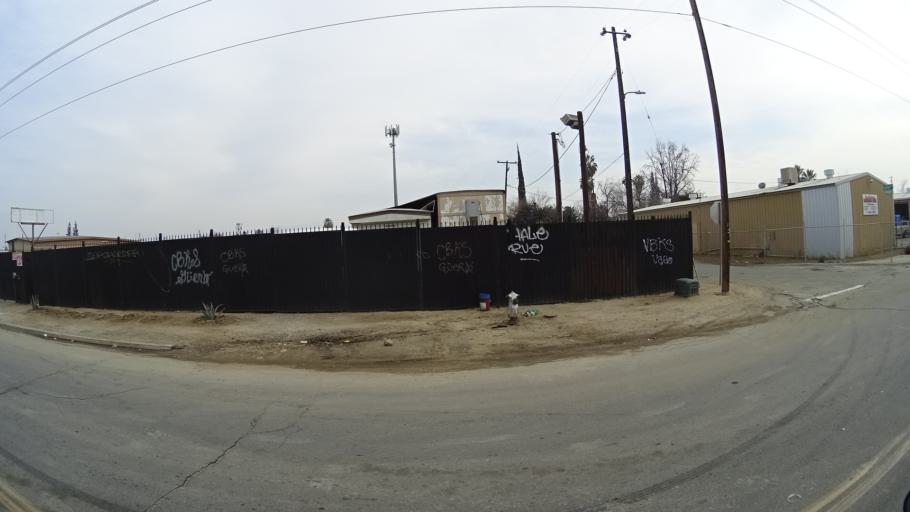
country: US
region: California
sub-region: Kern County
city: Bakersfield
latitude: 35.3704
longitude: -118.9764
